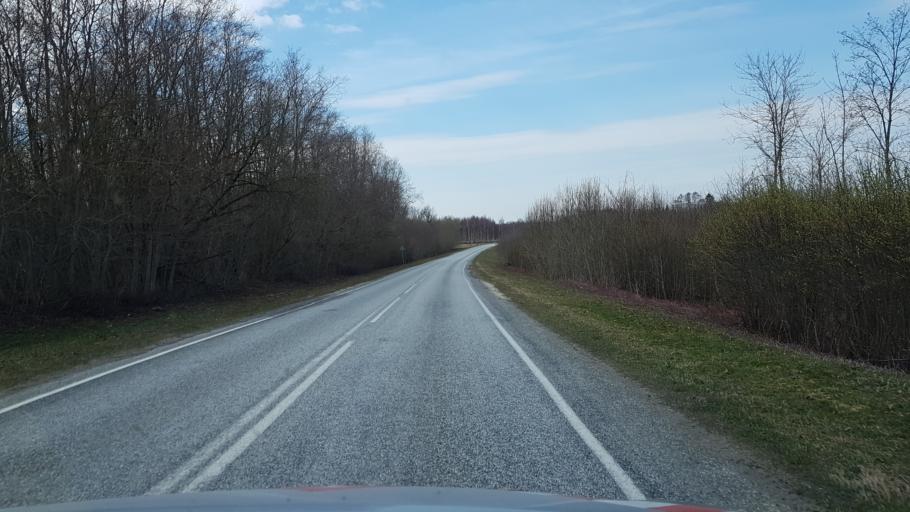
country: EE
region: Laeaene-Virumaa
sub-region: Haljala vald
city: Haljala
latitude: 59.4760
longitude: 26.1614
